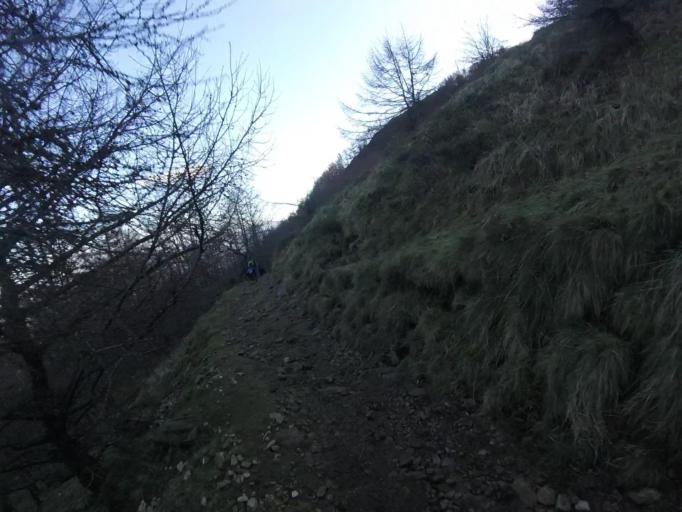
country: ES
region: Basque Country
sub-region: Provincia de Guipuzcoa
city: Irun
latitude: 43.2891
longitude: -1.7838
